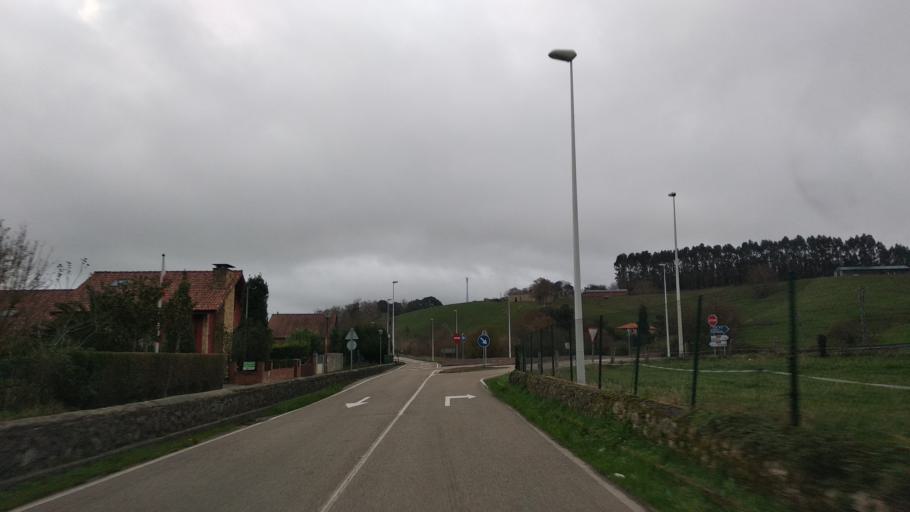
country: ES
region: Cantabria
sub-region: Provincia de Cantabria
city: Entrambasaguas
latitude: 43.4062
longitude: -3.7145
